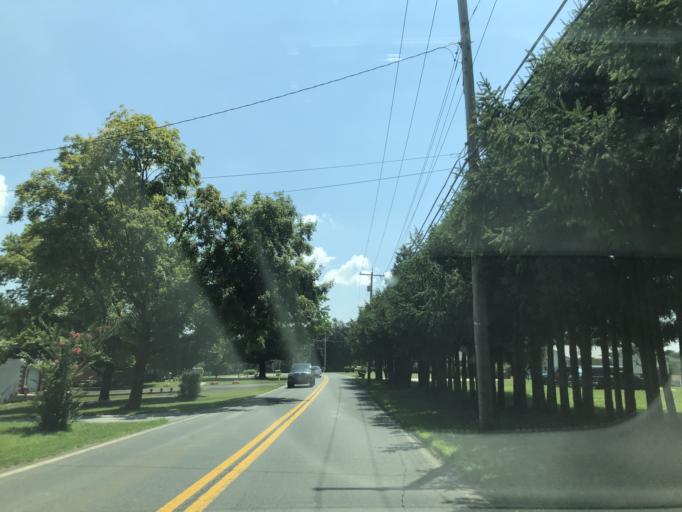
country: US
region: Maryland
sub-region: Carroll County
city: Westminster
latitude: 39.5390
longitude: -76.9779
